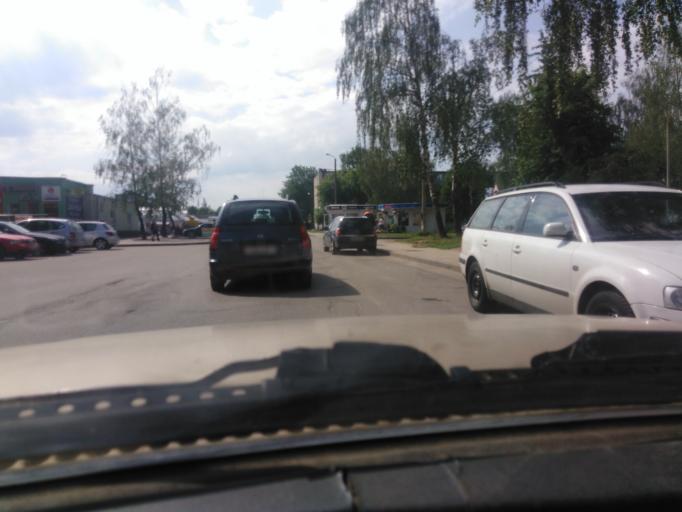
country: BY
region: Mogilev
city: Mahilyow
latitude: 53.9320
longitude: 30.3635
